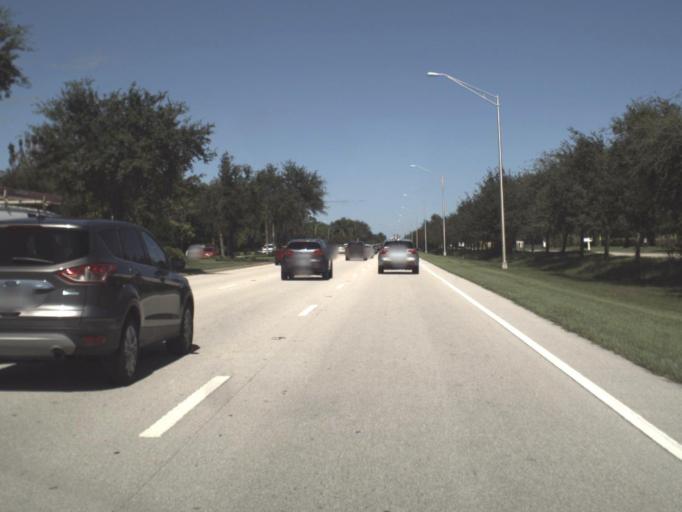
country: US
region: Florida
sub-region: Collier County
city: Pine Ridge
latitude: 26.2219
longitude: -81.8005
